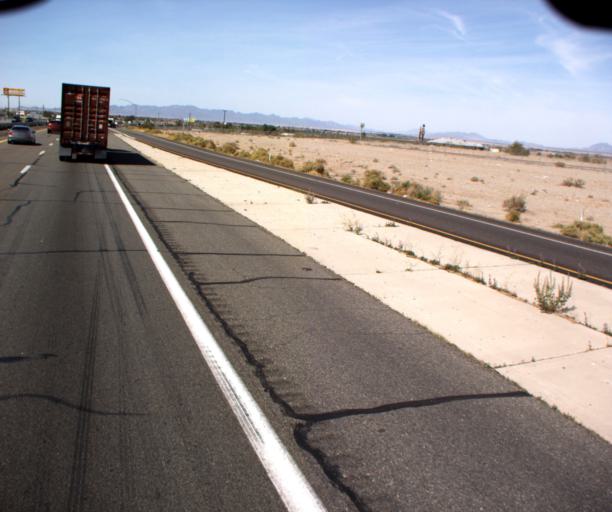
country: US
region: Arizona
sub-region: La Paz County
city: Ehrenberg
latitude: 33.6028
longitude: -114.5210
